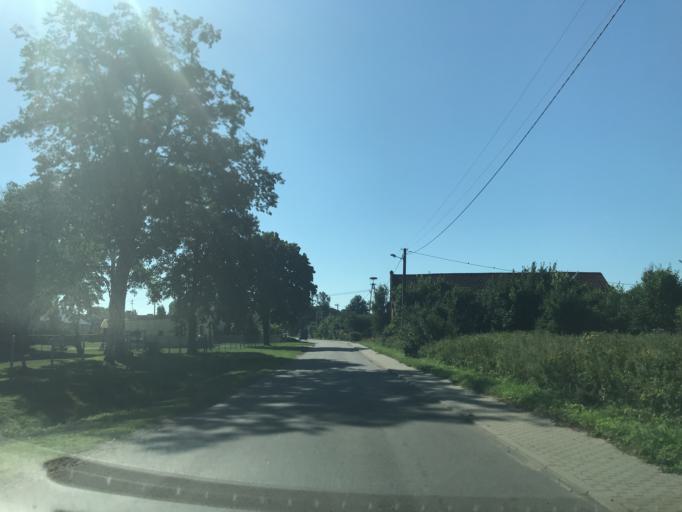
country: PL
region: Warmian-Masurian Voivodeship
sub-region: Powiat ostrodzki
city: Ostroda
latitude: 53.5959
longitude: 19.9020
